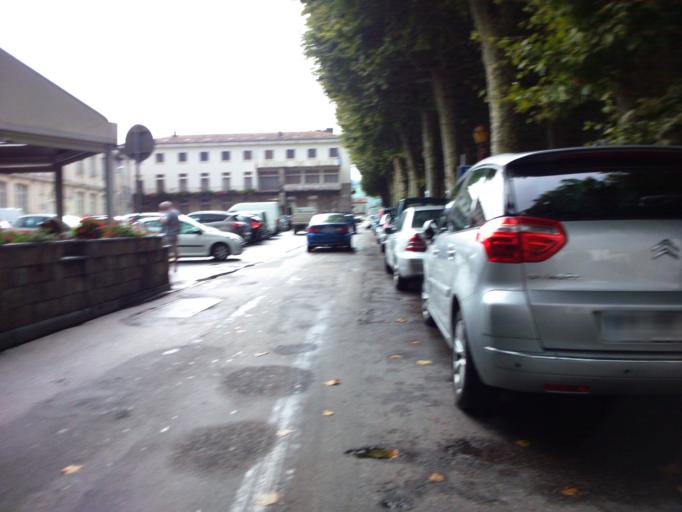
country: FR
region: Midi-Pyrenees
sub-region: Departement de l'Ariege
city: Saint-Girons
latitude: 42.9837
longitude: 1.1452
